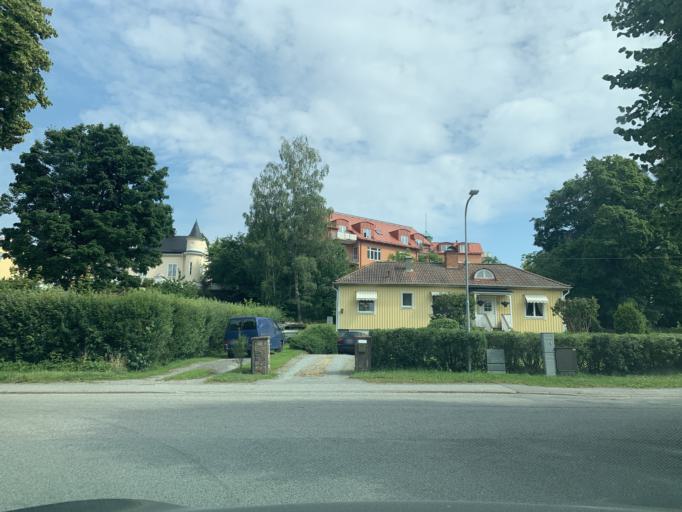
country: SE
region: Stockholm
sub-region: Norrtalje Kommun
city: Bergshamra
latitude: 59.4015
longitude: 18.0173
